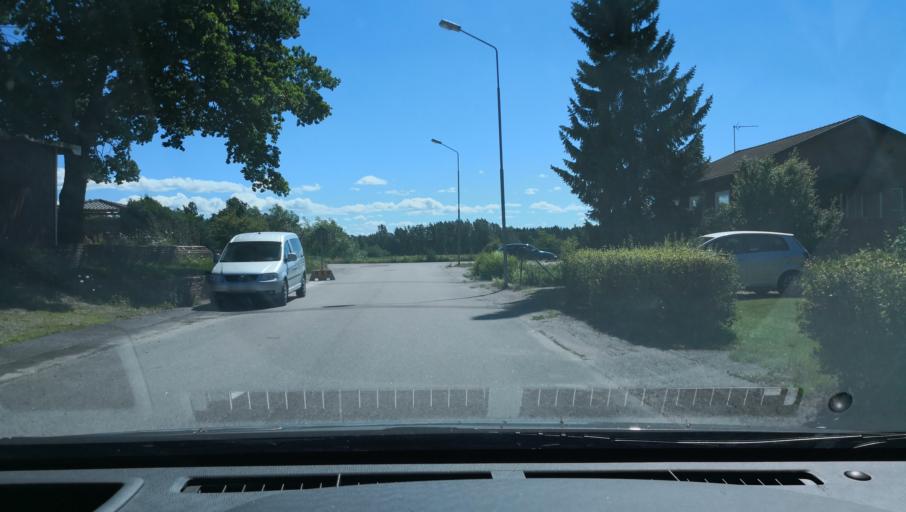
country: SE
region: Vaestmanland
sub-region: Kungsors Kommun
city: Kungsoer
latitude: 59.2775
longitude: 16.1111
